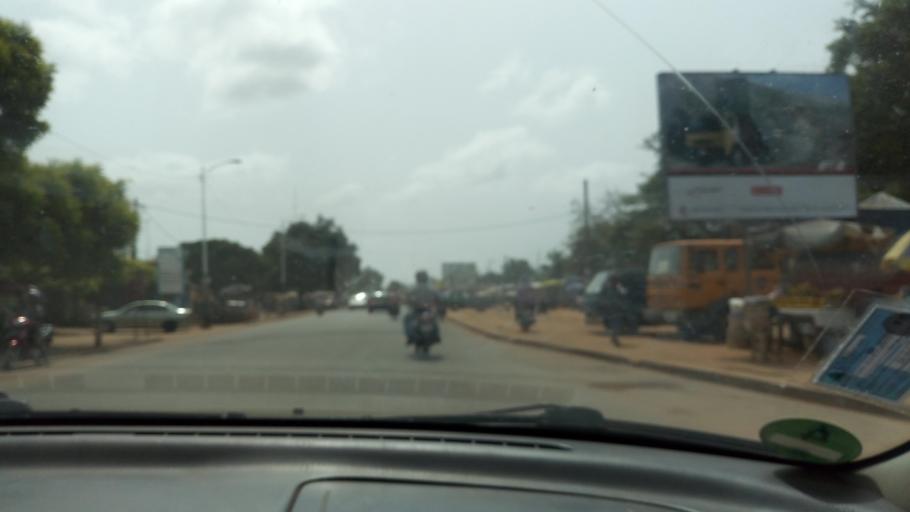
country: TG
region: Maritime
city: Lome
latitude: 6.1835
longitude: 1.1683
